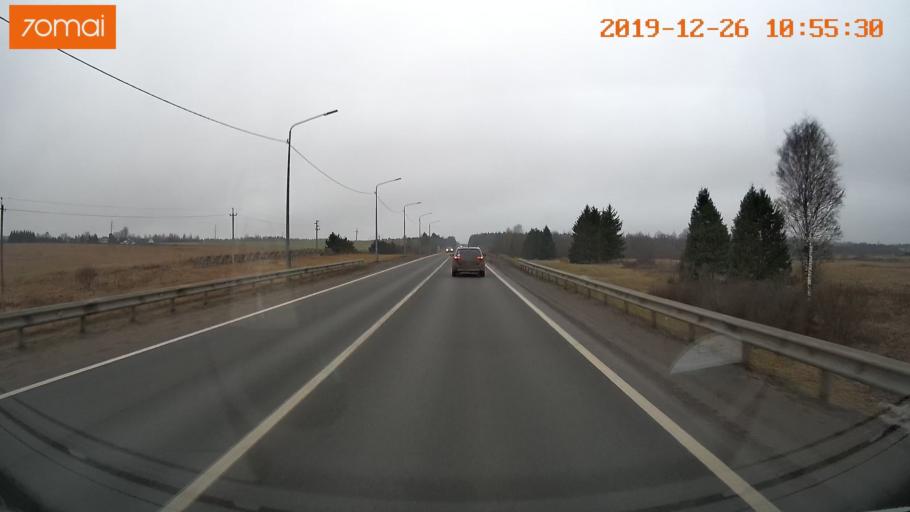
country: RU
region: Vologda
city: Molochnoye
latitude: 59.1898
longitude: 39.5828
